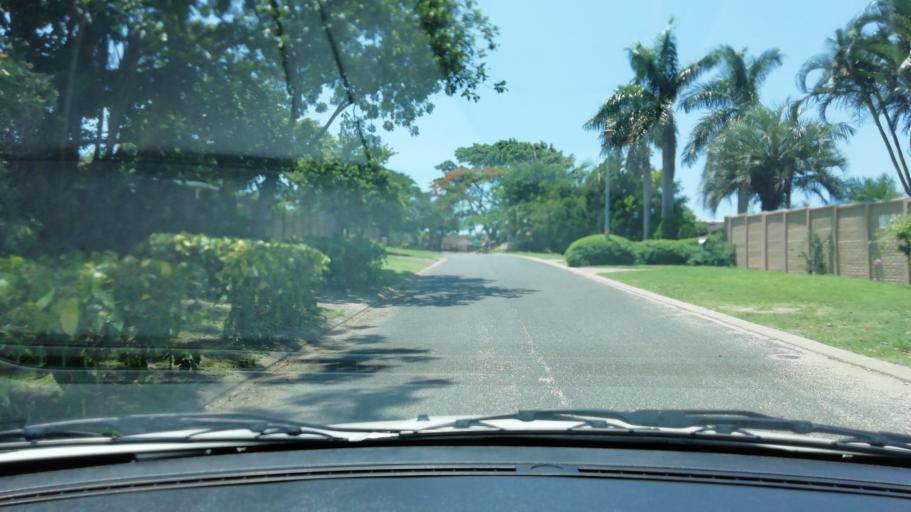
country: ZA
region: KwaZulu-Natal
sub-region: uThungulu District Municipality
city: Richards Bay
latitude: -28.7379
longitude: 32.0632
